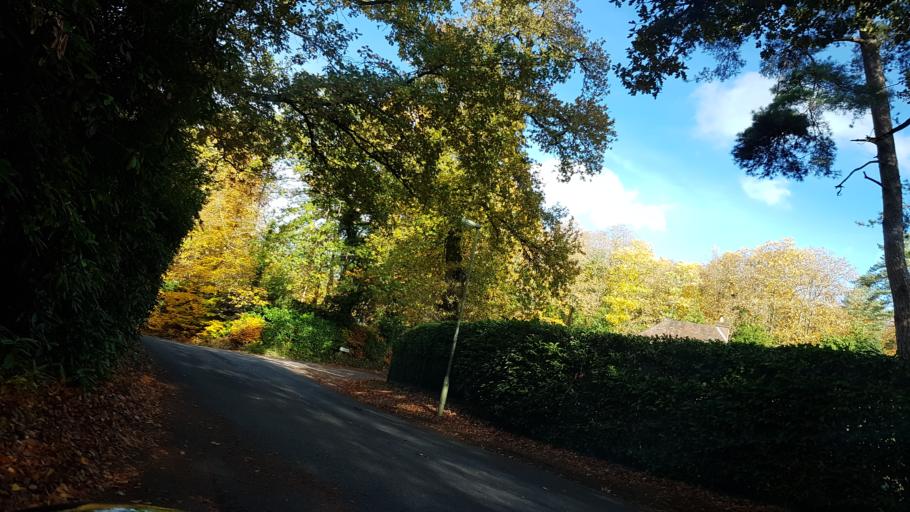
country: GB
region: England
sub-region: Surrey
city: Seale
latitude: 51.2073
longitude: -0.7493
